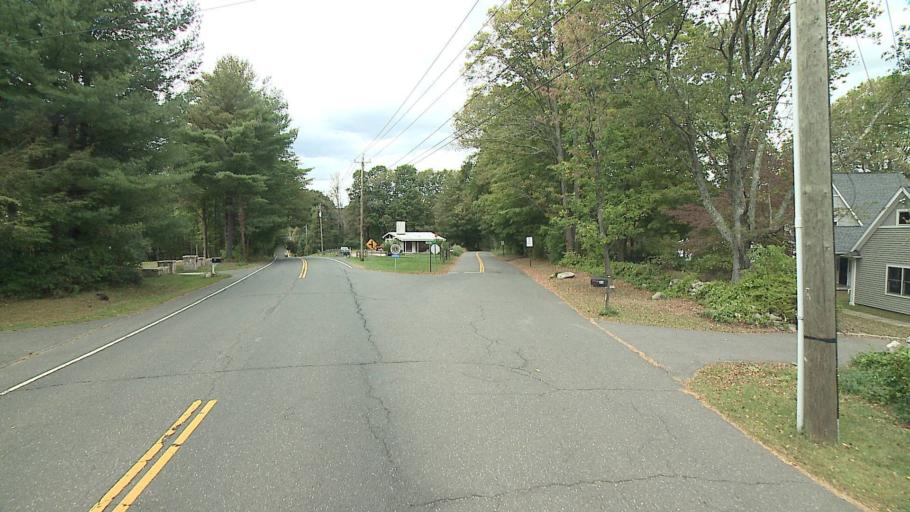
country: US
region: Connecticut
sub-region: Fairfield County
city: Ridgefield
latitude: 41.2478
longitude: -73.4865
